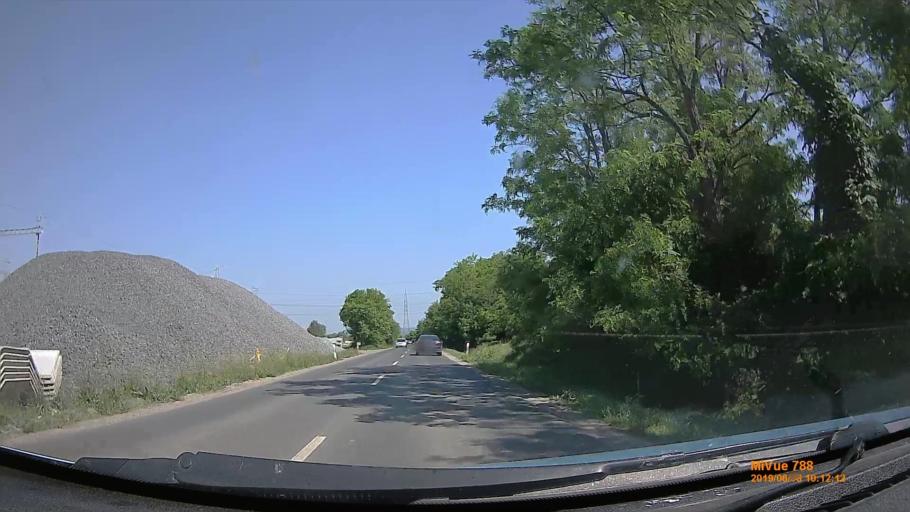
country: HU
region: Pest
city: Szazhalombatta
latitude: 47.3256
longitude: 18.8979
